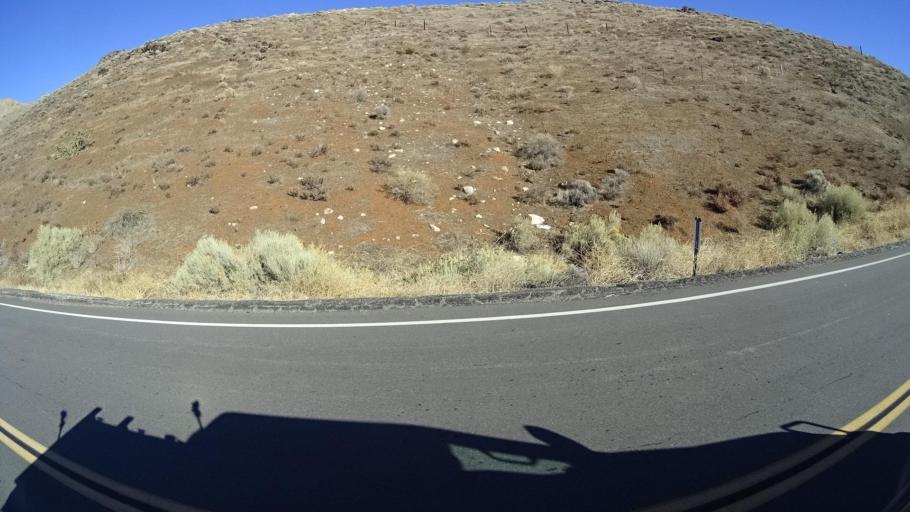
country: US
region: California
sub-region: Kern County
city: Wofford Heights
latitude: 35.6775
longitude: -118.4061
